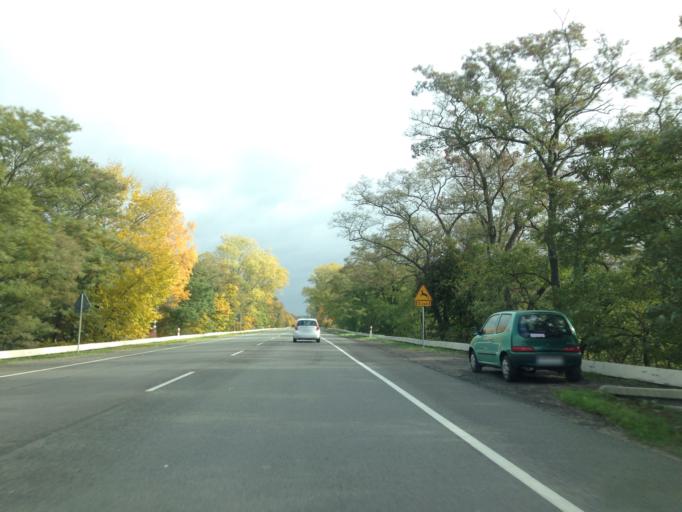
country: PL
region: Pomeranian Voivodeship
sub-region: Powiat malborski
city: Lisewo Malborskie
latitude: 54.0529
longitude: 18.8288
